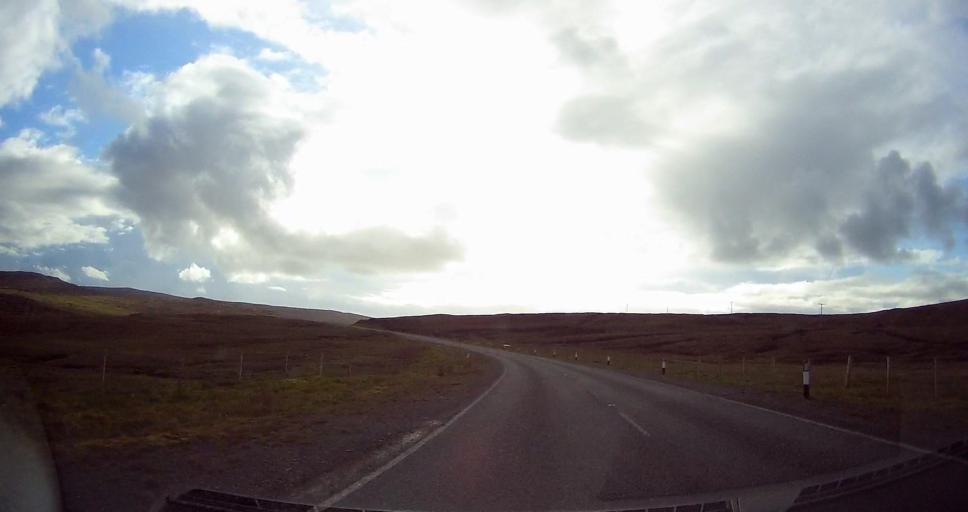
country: GB
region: Scotland
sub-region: Shetland Islands
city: Lerwick
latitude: 60.3492
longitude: -1.2145
